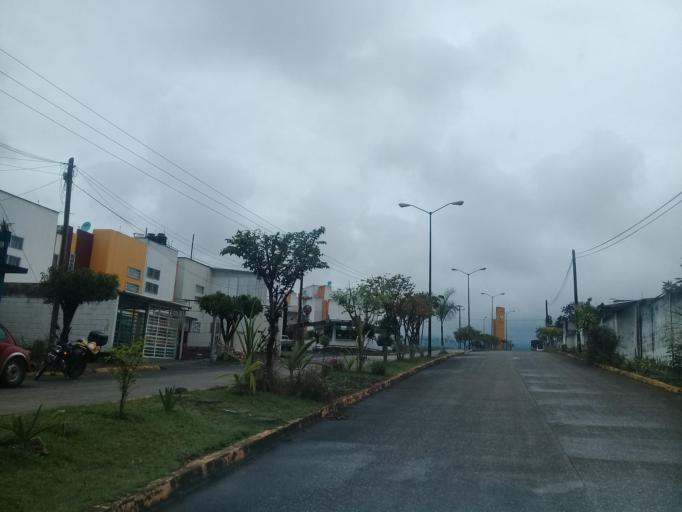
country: MX
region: Veracruz
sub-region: Cordoba
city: San Jose de Tapia
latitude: 18.8374
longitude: -96.9549
